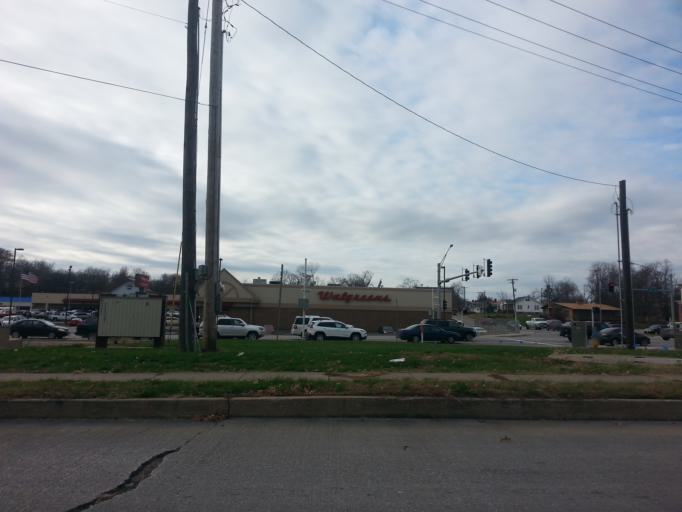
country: US
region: Missouri
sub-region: Marion County
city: Hannibal
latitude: 39.7127
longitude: -91.3910
